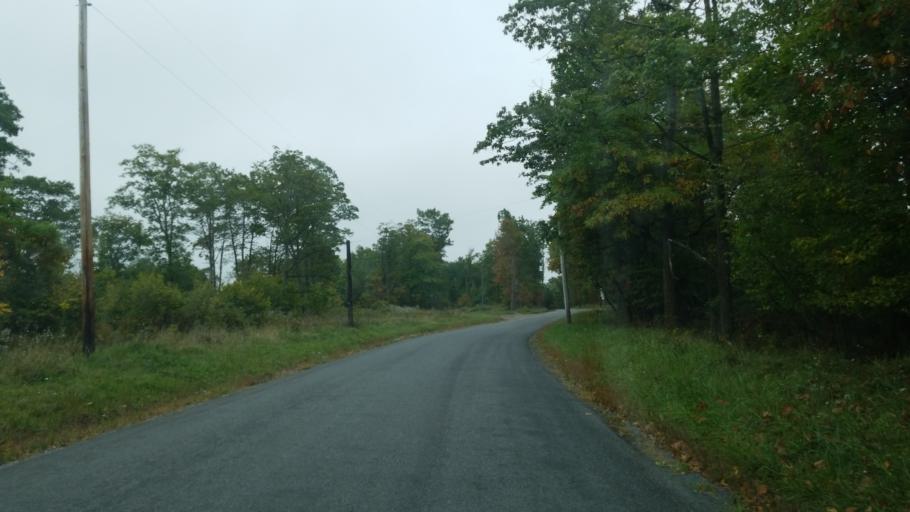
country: US
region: Pennsylvania
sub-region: Clearfield County
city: Curwensville
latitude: 41.0314
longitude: -78.5583
